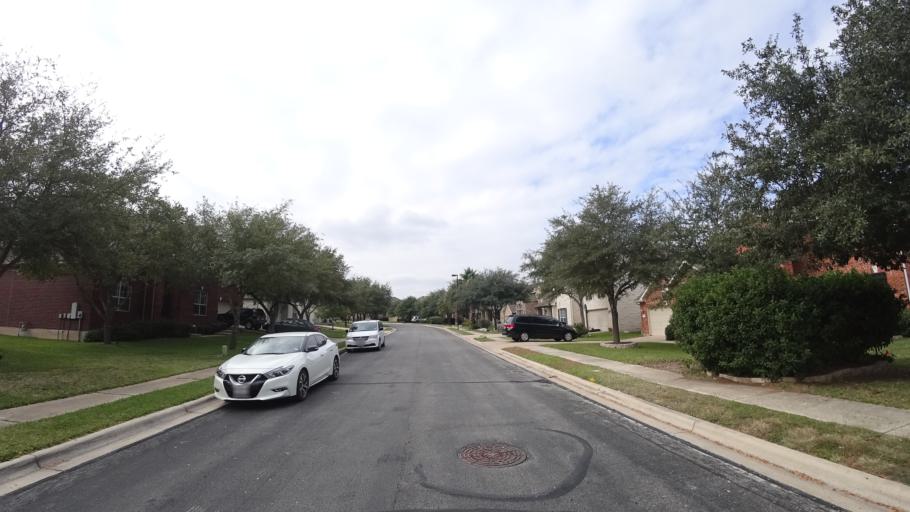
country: US
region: Texas
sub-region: Travis County
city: Shady Hollow
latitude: 30.1921
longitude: -97.9007
